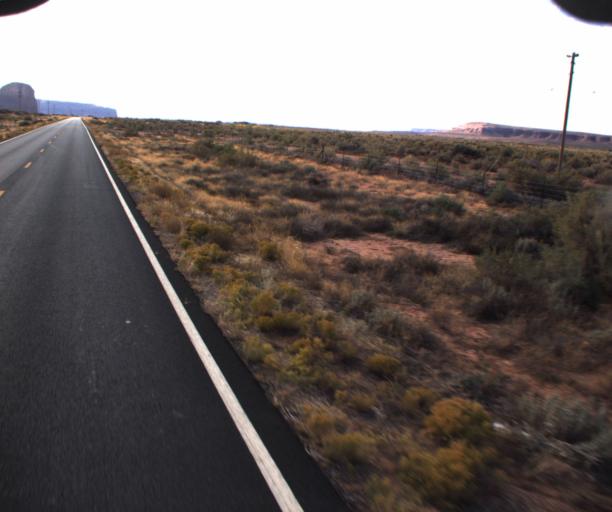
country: US
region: Arizona
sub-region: Apache County
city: Many Farms
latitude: 36.6876
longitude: -109.6077
